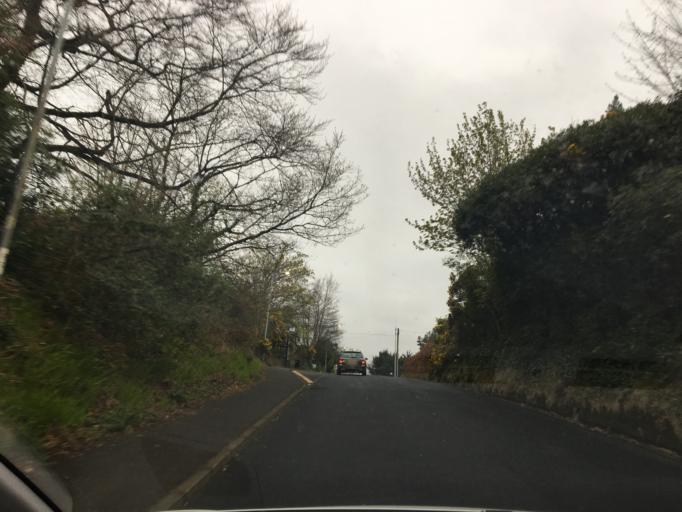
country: GB
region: Scotland
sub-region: North Ayrshire
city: Lamlash
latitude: 55.5392
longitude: -5.1226
